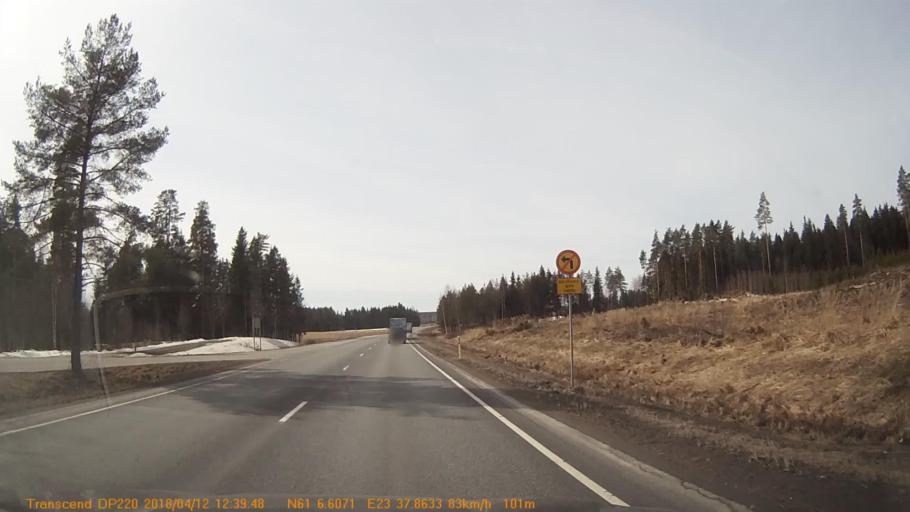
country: FI
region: Pirkanmaa
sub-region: Etelae-Pirkanmaa
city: Kylmaekoski
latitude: 61.1100
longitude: 23.6305
